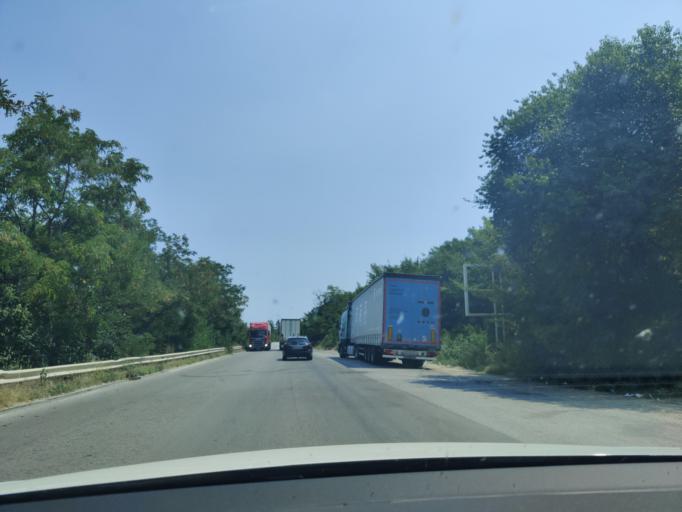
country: BG
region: Montana
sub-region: Obshtina Montana
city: Montana
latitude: 43.4272
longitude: 23.1523
